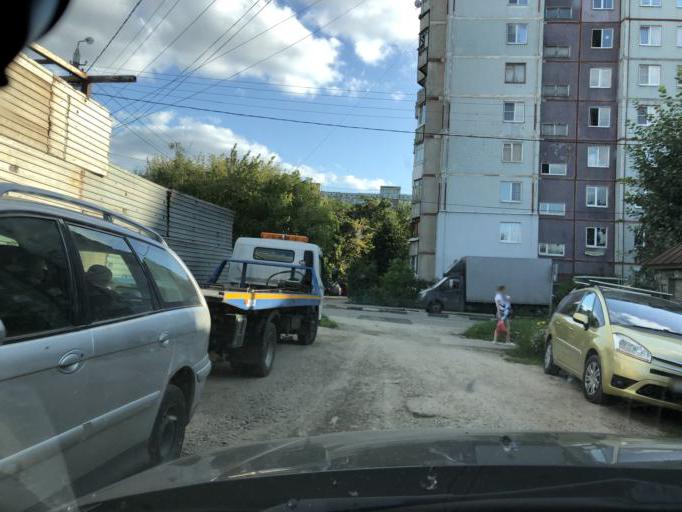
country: RU
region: Tula
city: Tula
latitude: 54.2110
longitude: 37.6061
